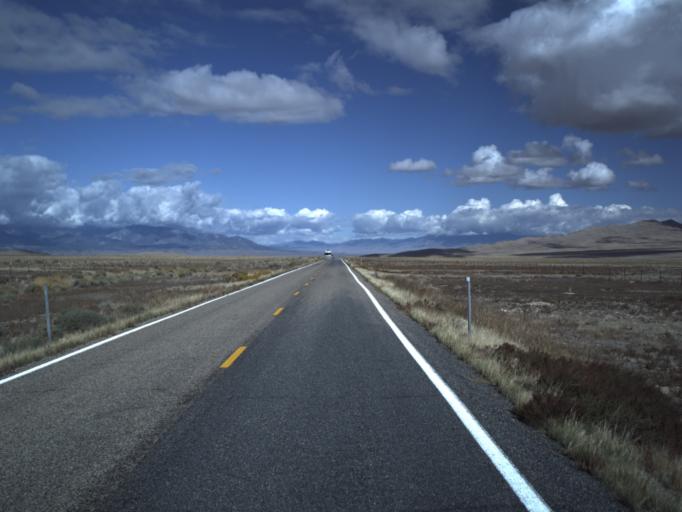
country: US
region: Utah
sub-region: Beaver County
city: Milford
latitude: 38.6674
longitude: -113.8822
